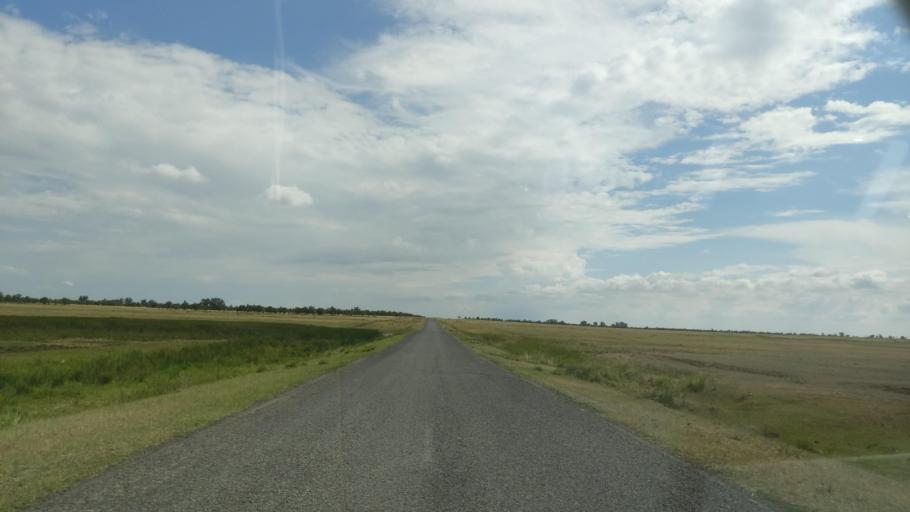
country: KZ
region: Pavlodar
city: Pavlodar
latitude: 52.6362
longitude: 76.9527
